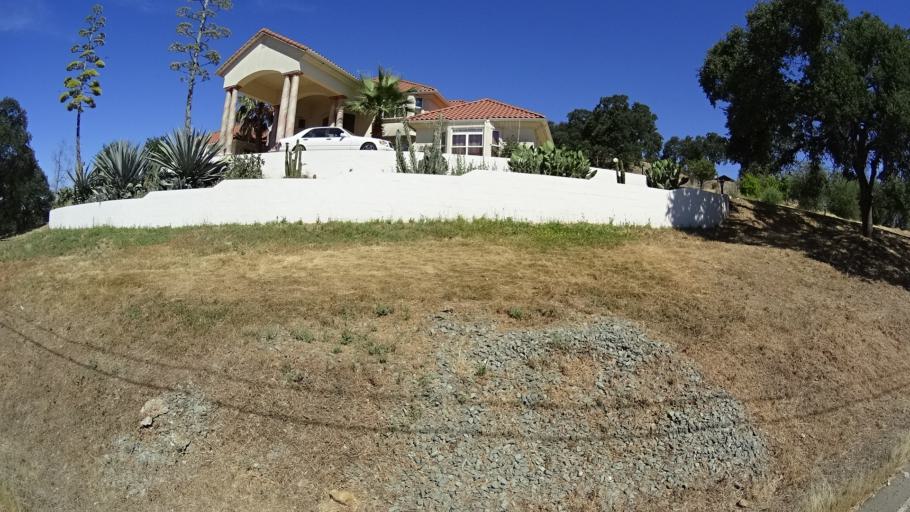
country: US
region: California
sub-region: Calaveras County
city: Rancho Calaveras
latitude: 38.1438
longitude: -120.8566
